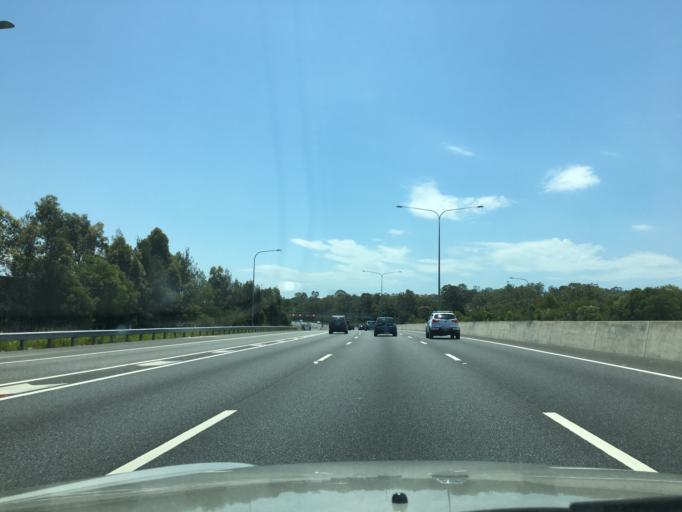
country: AU
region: Queensland
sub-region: Brisbane
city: Belmont
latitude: -27.4992
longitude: 153.1257
